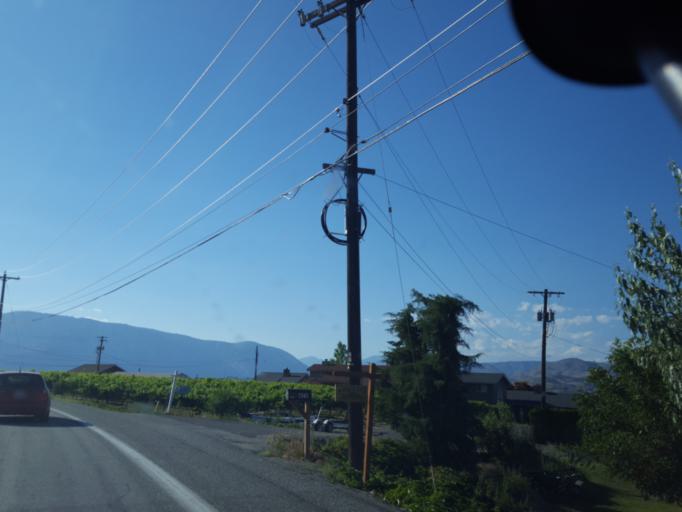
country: US
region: Washington
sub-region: Chelan County
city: Manson
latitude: 47.8429
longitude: -120.0962
